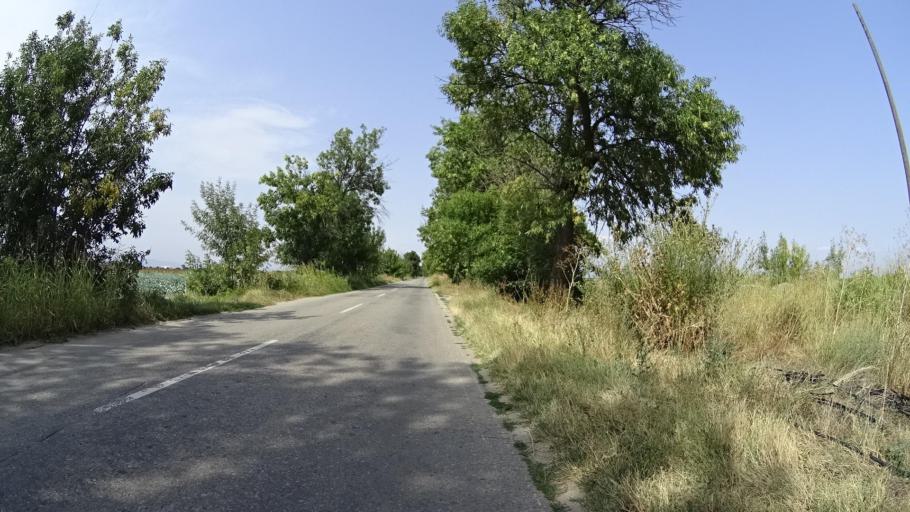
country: BG
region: Plovdiv
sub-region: Obshtina Plovdiv
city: Plovdiv
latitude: 42.2521
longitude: 24.7979
